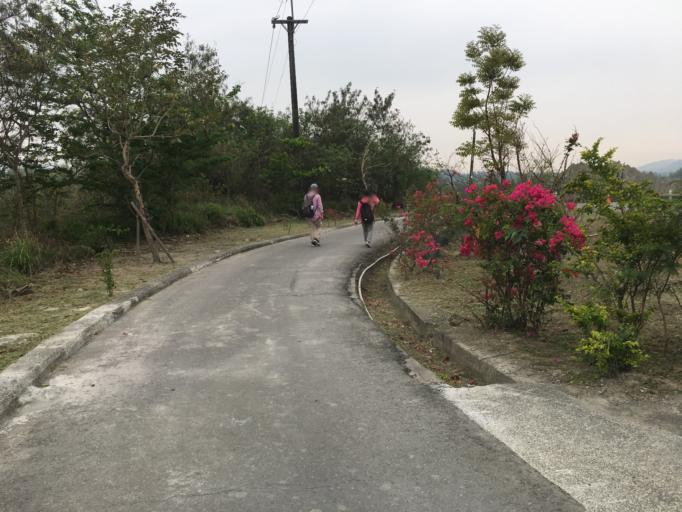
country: TW
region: Taiwan
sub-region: Tainan
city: Tainan
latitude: 22.8876
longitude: 120.3889
